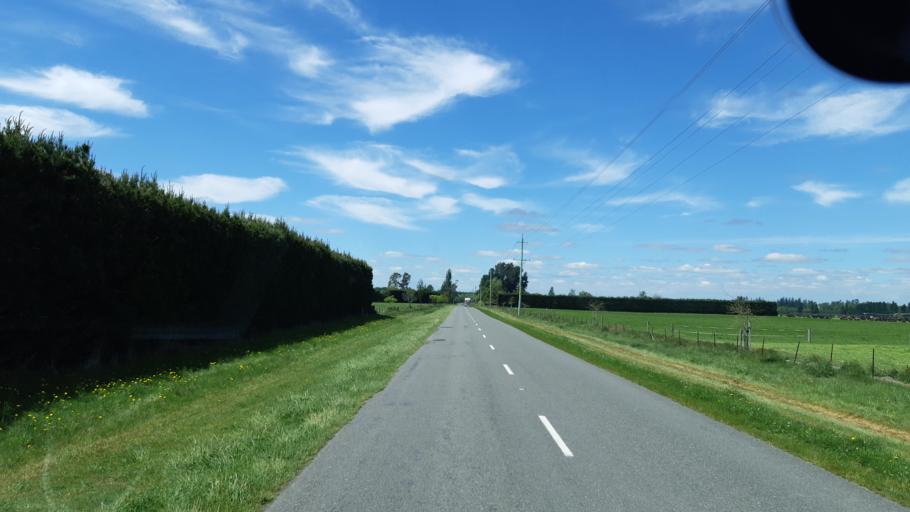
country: NZ
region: Canterbury
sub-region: Ashburton District
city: Methven
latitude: -43.7294
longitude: 171.5101
